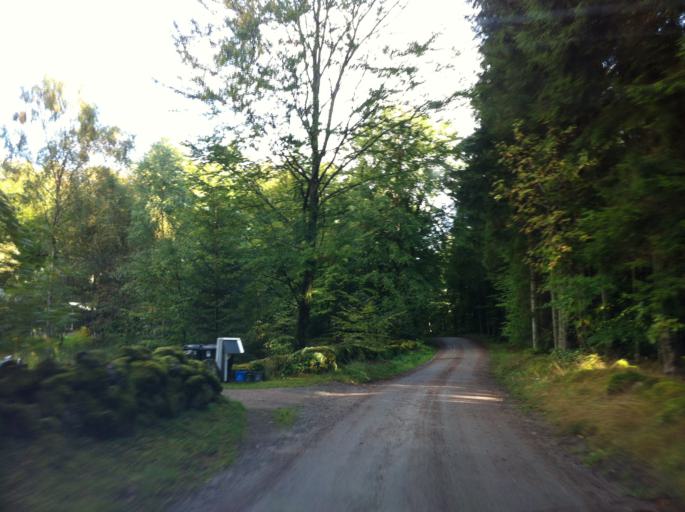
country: SE
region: Skane
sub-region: Hassleholms Kommun
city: Sosdala
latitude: 56.1298
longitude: 13.5840
